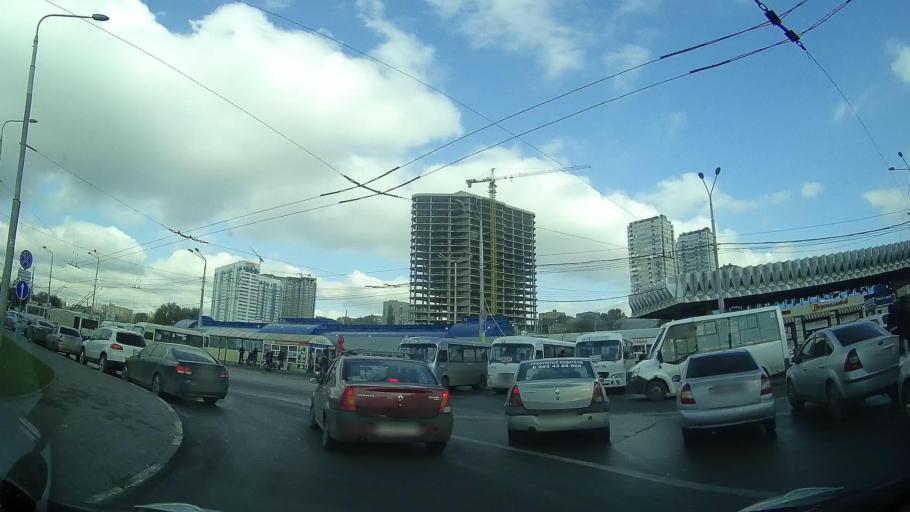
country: RU
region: Rostov
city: Rostov-na-Donu
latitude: 47.2201
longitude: 39.6921
